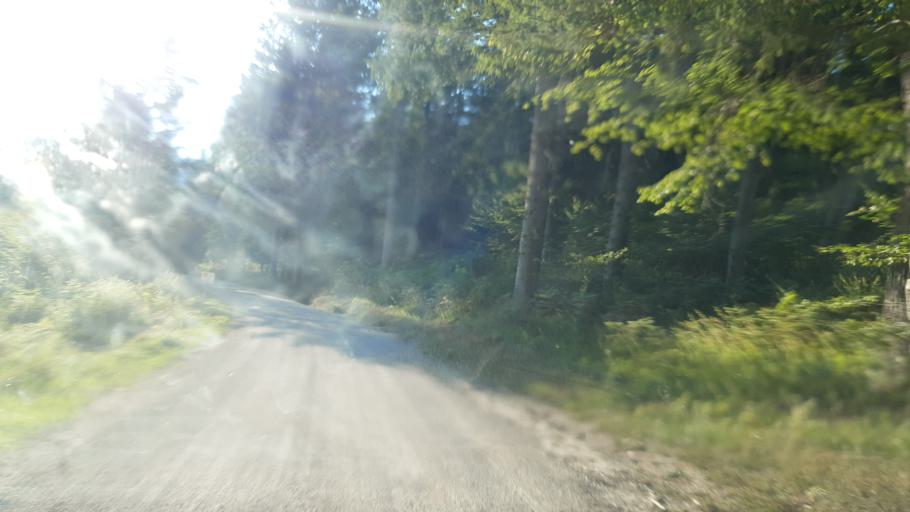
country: SI
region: Dolenjske Toplice
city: Dolenjske Toplice
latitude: 45.7159
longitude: 15.0236
